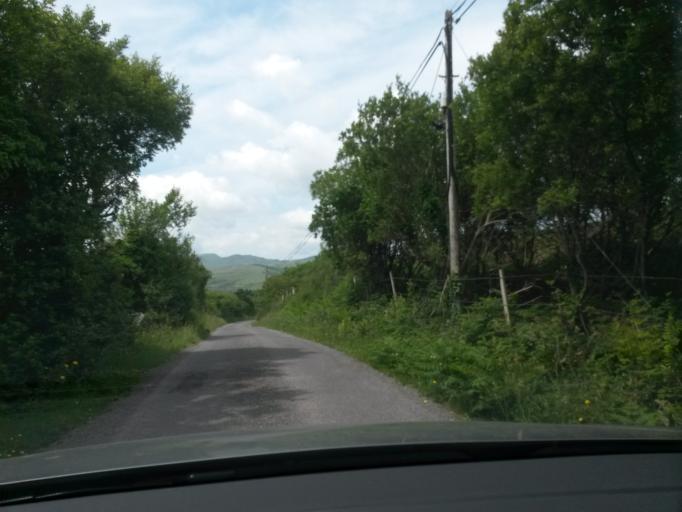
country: IE
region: Munster
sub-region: Ciarrai
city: Cahersiveen
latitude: 51.7990
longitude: -9.9616
